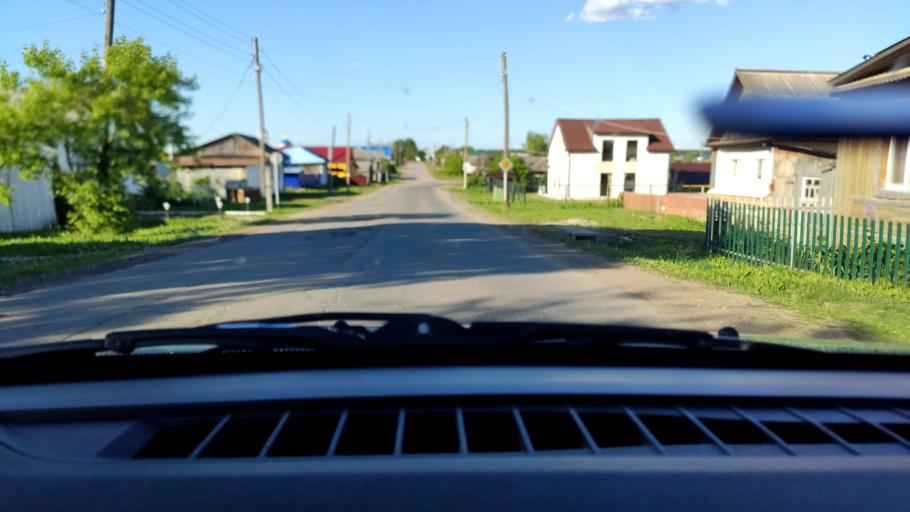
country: RU
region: Perm
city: Orda
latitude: 57.1916
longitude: 56.8925
